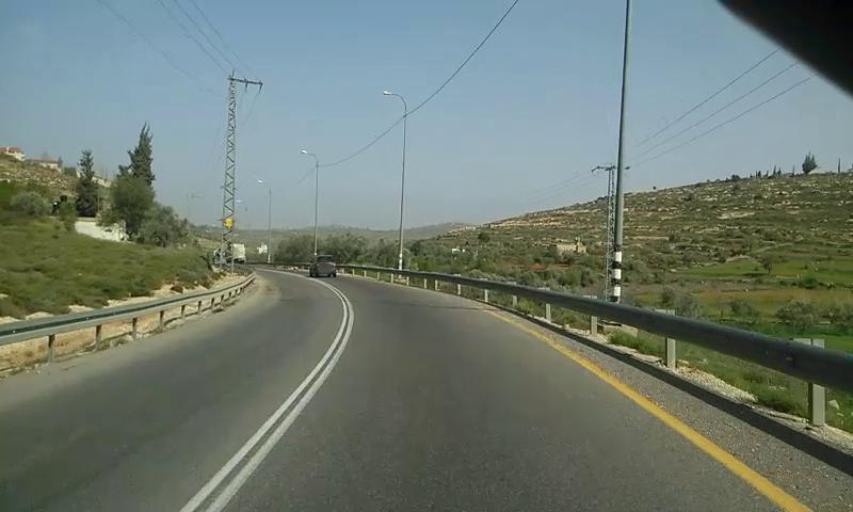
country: PS
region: West Bank
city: Sinjil
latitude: 32.0309
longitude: 35.2716
